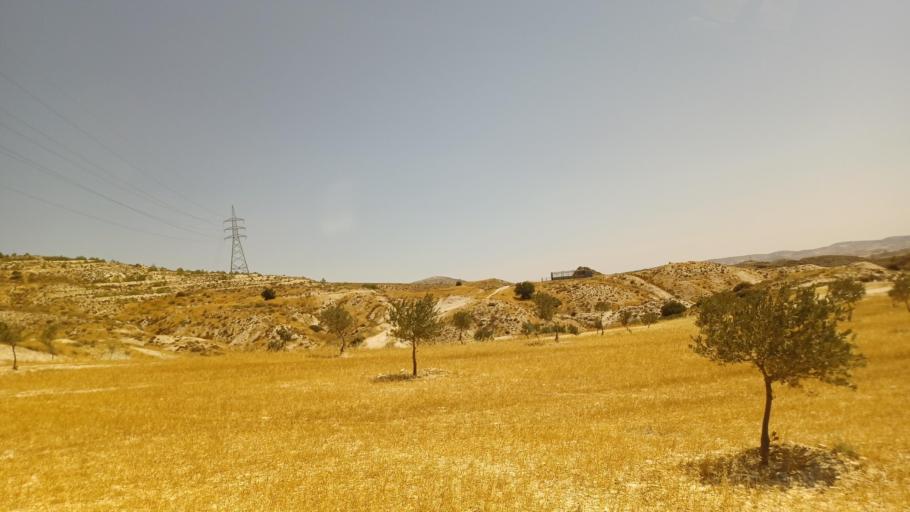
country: CY
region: Larnaka
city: Athienou
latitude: 35.0083
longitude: 33.5529
